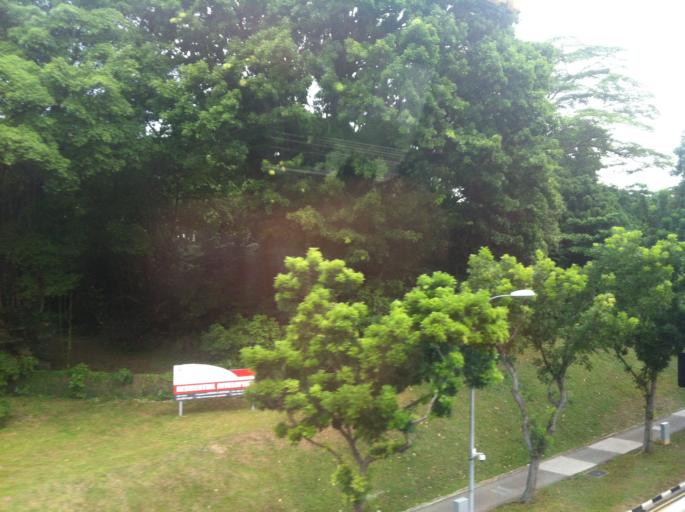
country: SG
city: Singapore
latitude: 1.3267
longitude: 103.9455
